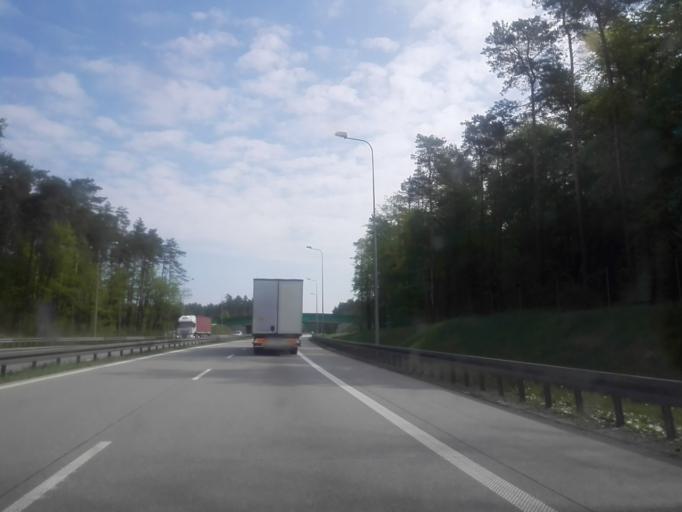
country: PL
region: Lodz Voivodeship
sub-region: Powiat skierniewicki
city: Kowiesy
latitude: 51.9274
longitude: 20.4649
